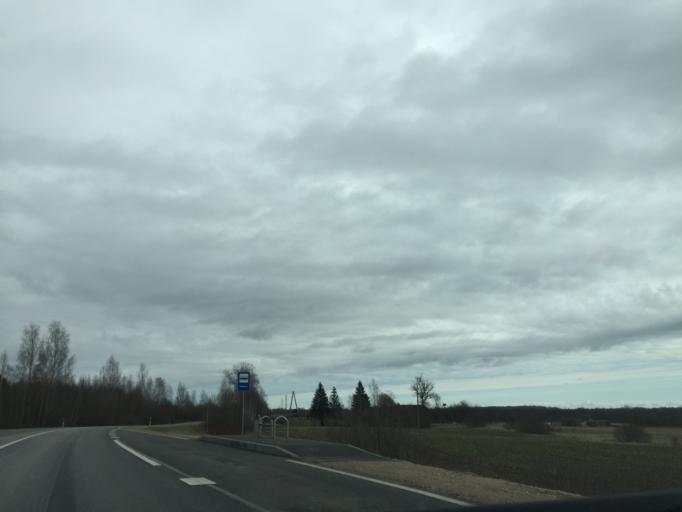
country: LV
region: Daugavpils
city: Daugavpils
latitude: 55.9257
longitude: 26.6848
